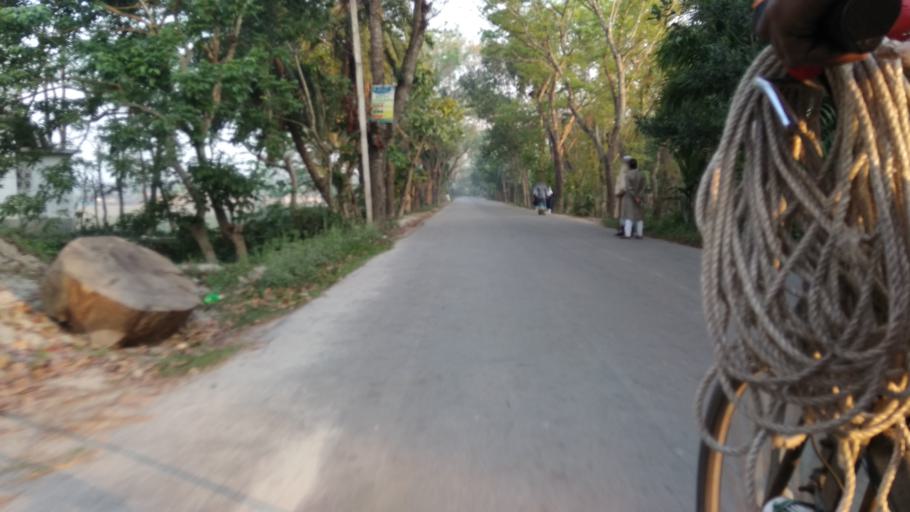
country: BD
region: Barisal
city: Mehendiganj
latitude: 22.9188
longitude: 90.4098
